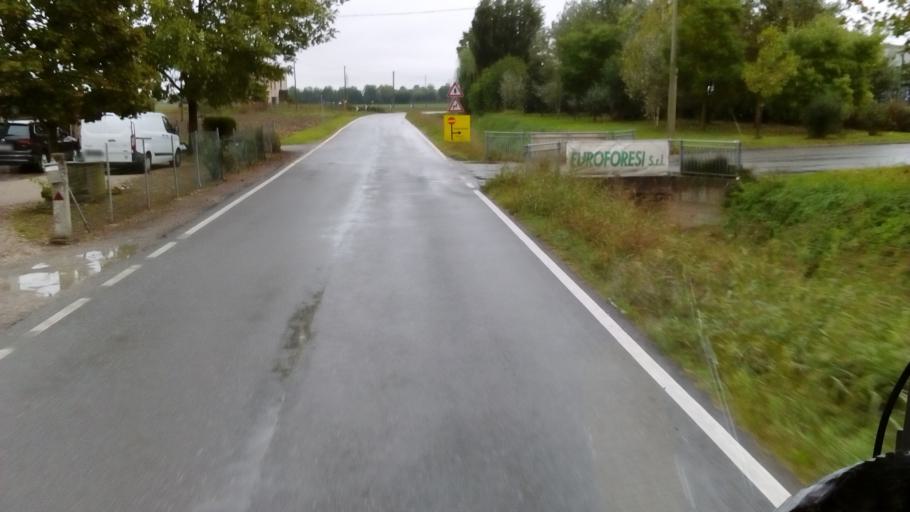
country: IT
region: Emilia-Romagna
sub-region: Provincia di Reggio Emilia
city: Luzzara
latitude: 44.9504
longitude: 10.7039
